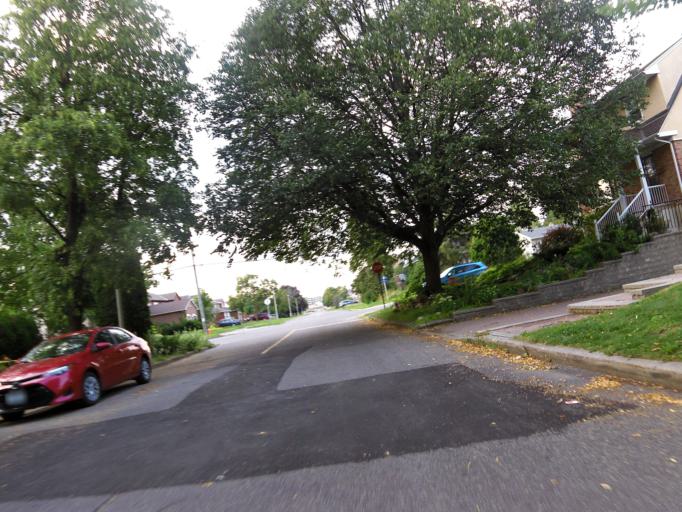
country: CA
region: Ontario
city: Ottawa
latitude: 45.3683
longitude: -75.7665
